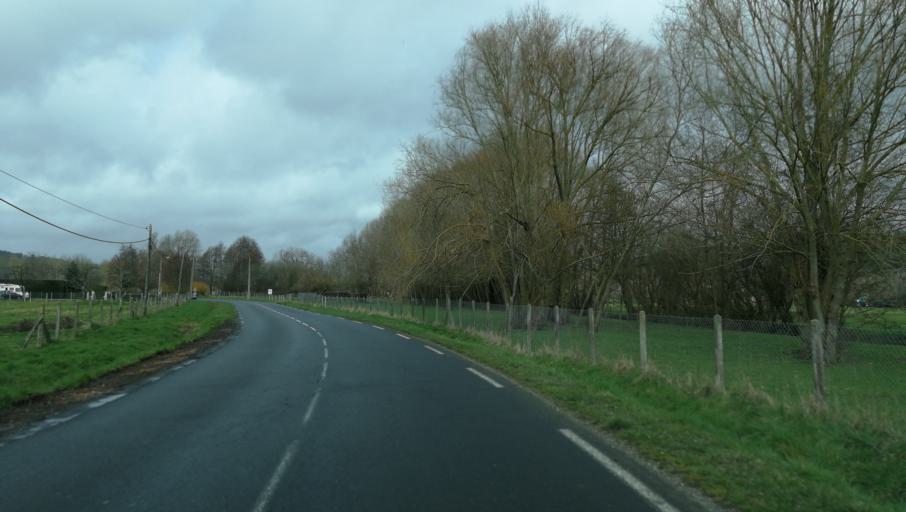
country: FR
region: Haute-Normandie
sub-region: Departement de l'Eure
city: Brionne
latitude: 49.2115
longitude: 0.7100
